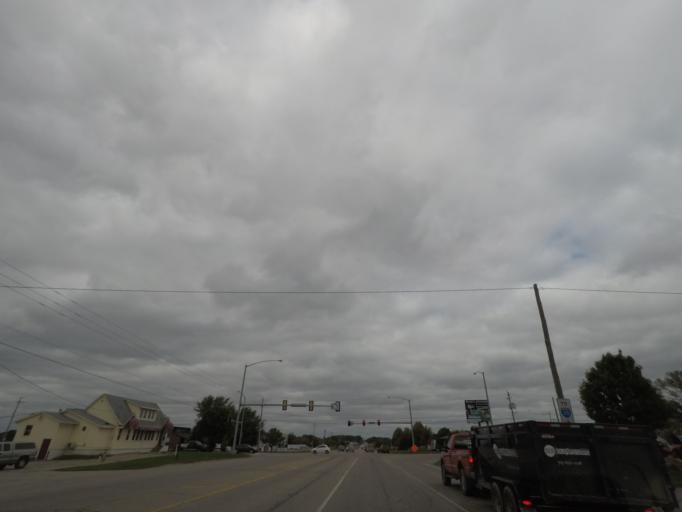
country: US
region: Iowa
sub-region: Polk County
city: Saylorville
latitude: 41.6798
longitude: -93.6006
